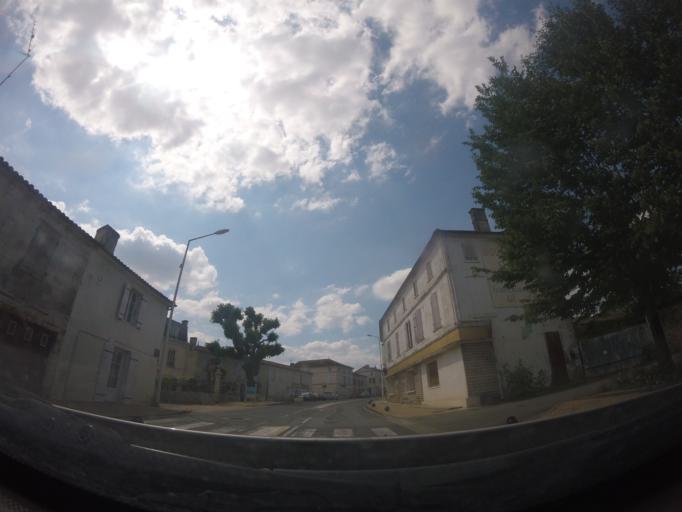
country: FR
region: Poitou-Charentes
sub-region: Departement de la Charente-Maritime
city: Bords
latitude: 45.8604
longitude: -0.8358
